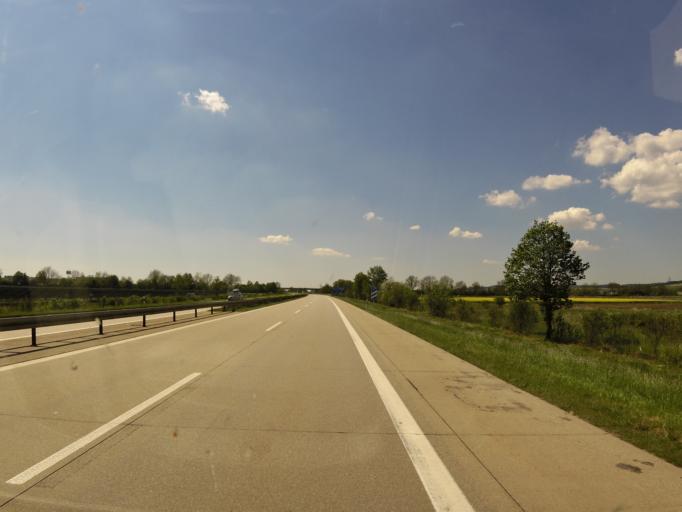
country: DE
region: Bavaria
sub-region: Lower Bavaria
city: Dingolfing
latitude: 48.6584
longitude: 12.4797
